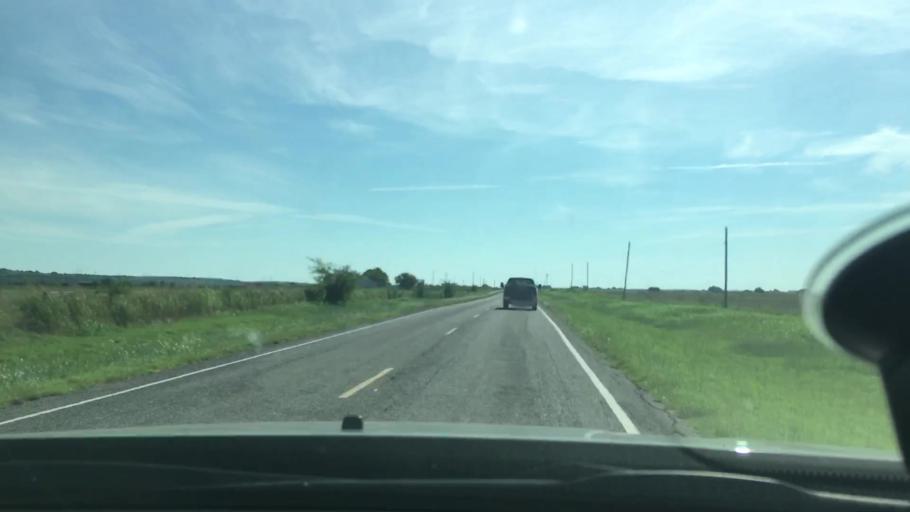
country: US
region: Oklahoma
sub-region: Carter County
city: Lone Grove
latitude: 34.3327
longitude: -97.2554
